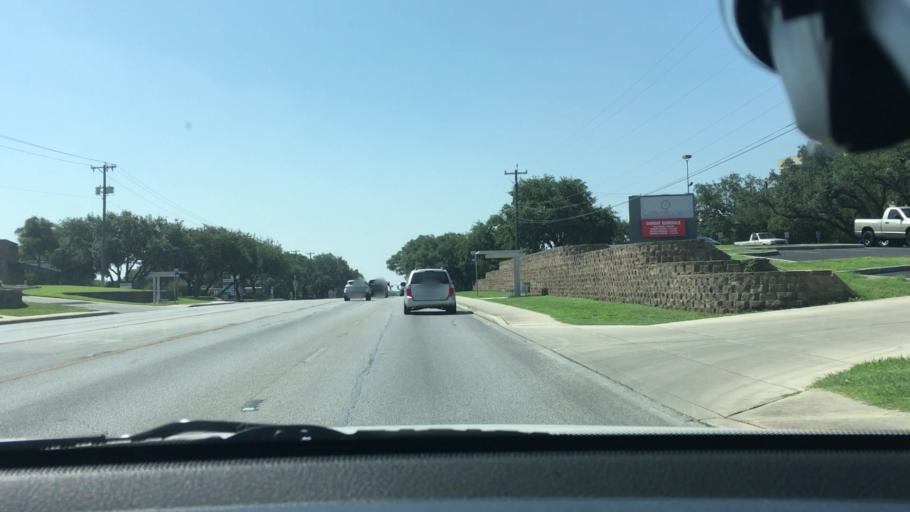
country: US
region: Texas
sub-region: Bexar County
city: Castle Hills
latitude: 29.5355
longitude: -98.5247
